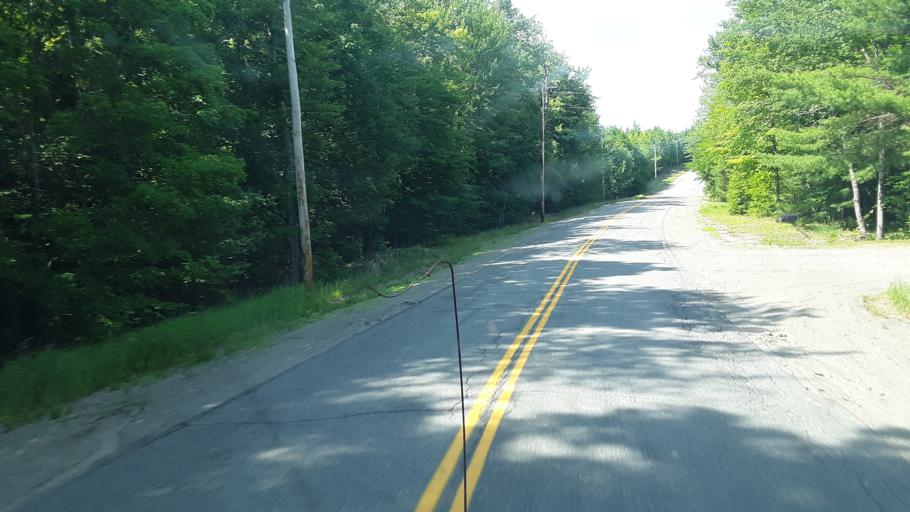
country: US
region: Maine
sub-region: Washington County
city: Calais
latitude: 45.1074
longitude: -67.5083
